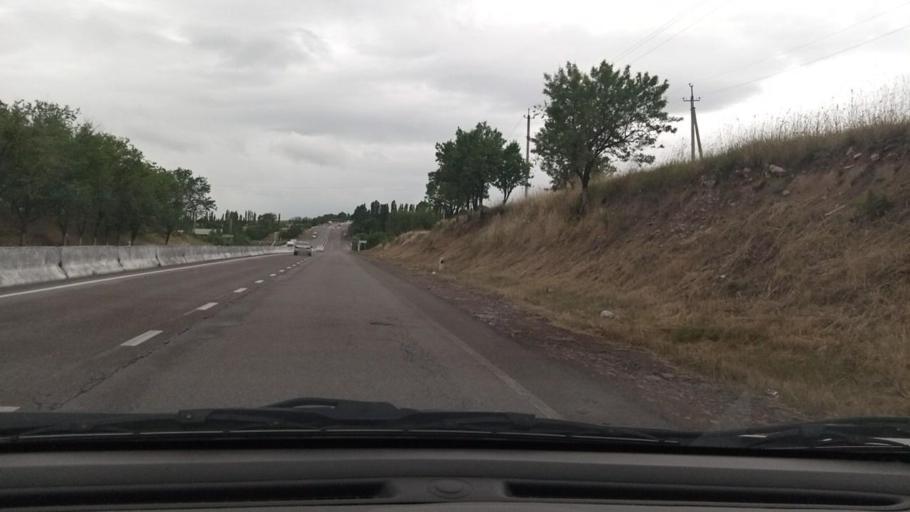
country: UZ
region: Toshkent
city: Angren
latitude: 40.9635
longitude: 69.9495
